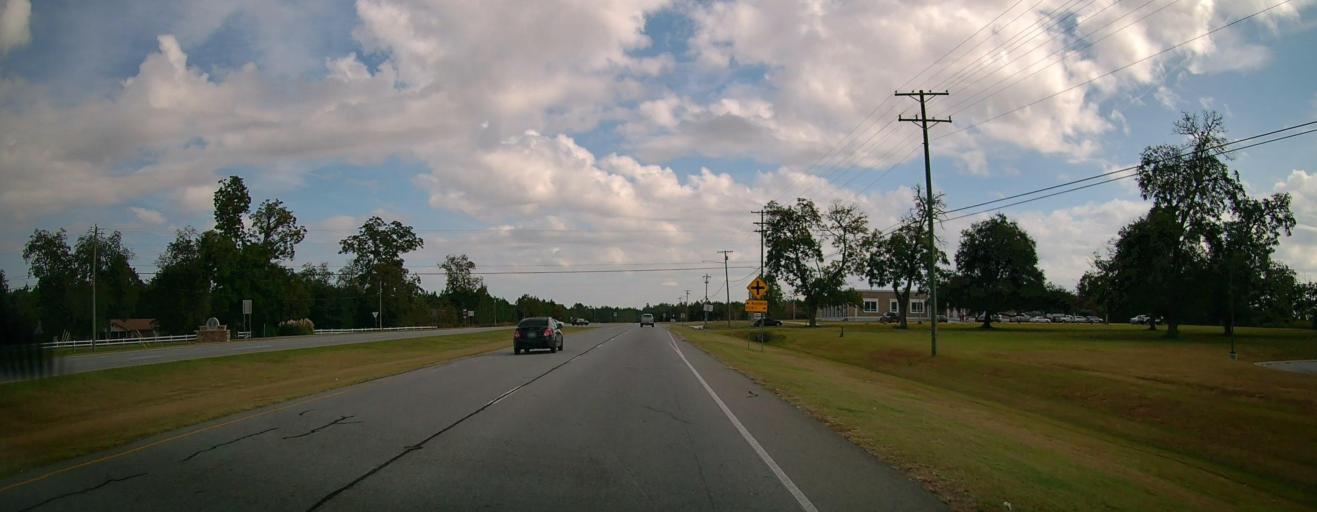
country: US
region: Georgia
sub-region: Mitchell County
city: Camilla
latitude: 31.2193
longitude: -84.1888
